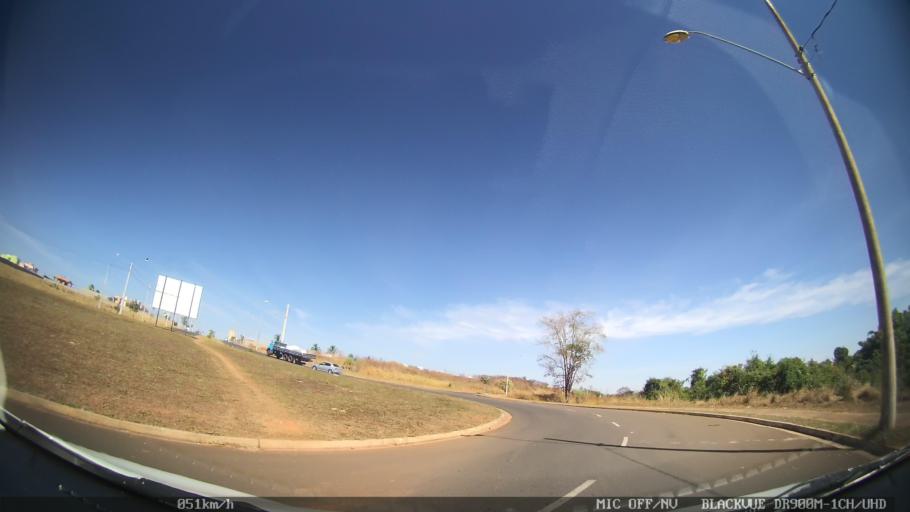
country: BR
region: Sao Paulo
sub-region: Sao Jose Do Rio Preto
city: Sao Jose do Rio Preto
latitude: -20.7619
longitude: -49.4203
